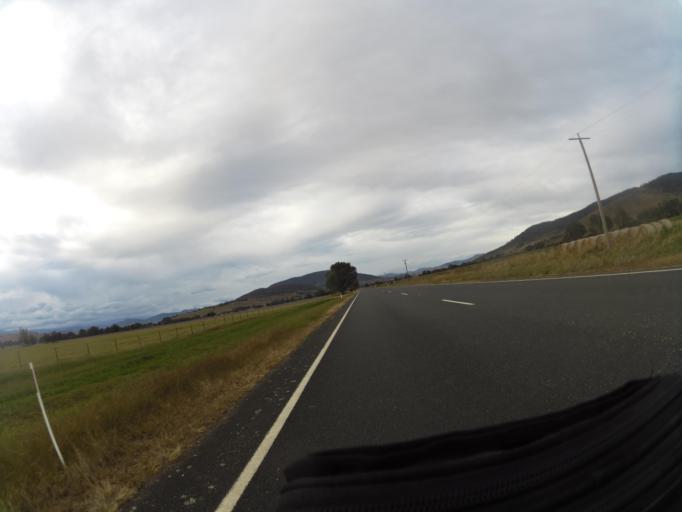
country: AU
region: New South Wales
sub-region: Snowy River
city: Jindabyne
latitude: -36.1010
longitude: 147.9810
